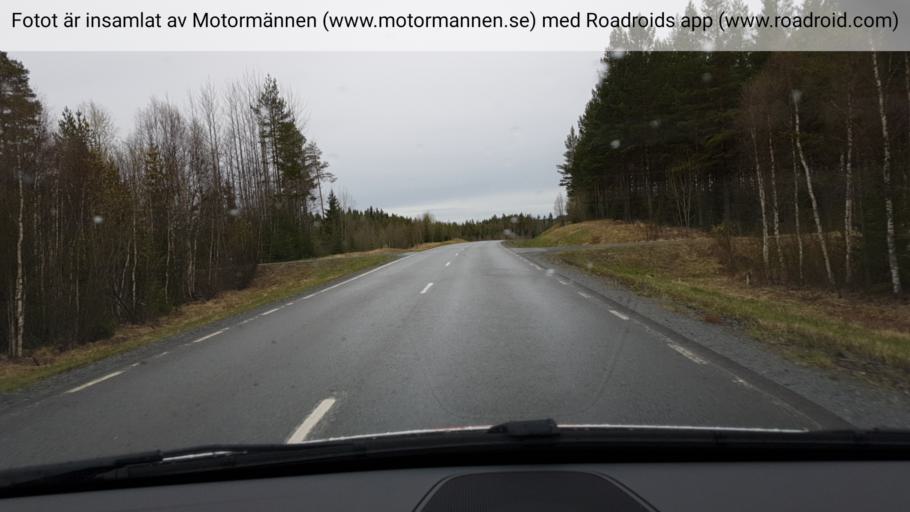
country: SE
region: Jaemtland
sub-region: Krokoms Kommun
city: Krokom
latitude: 63.2778
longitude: 14.4411
